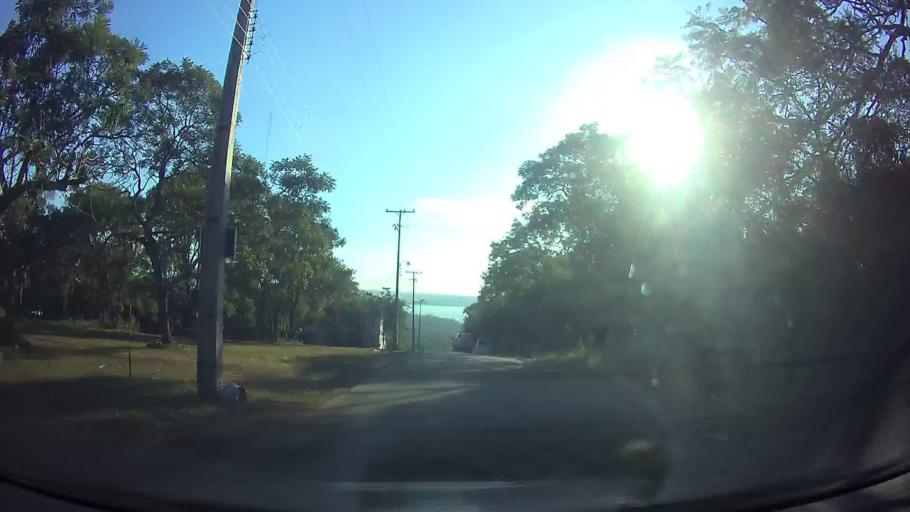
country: PY
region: Cordillera
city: San Bernardino
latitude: -25.3148
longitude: -57.2651
